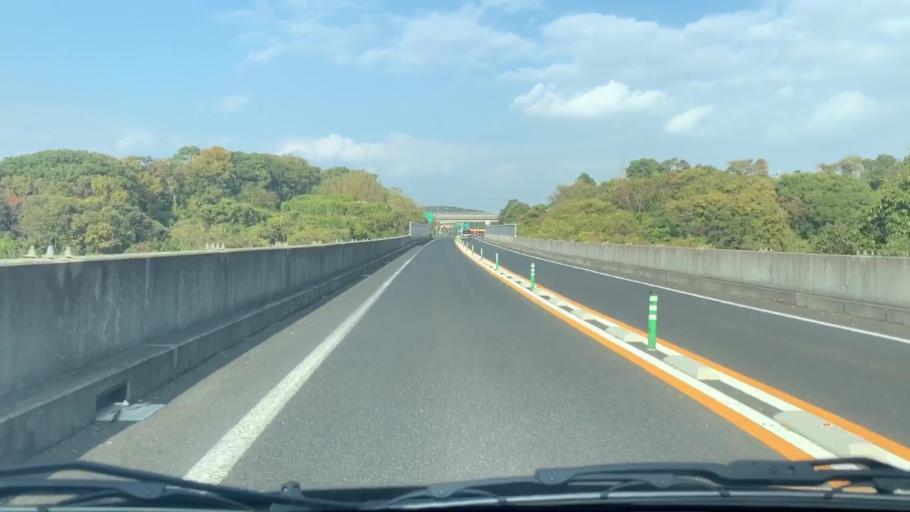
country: JP
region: Nagasaki
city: Sasebo
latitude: 33.0615
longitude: 129.7595
